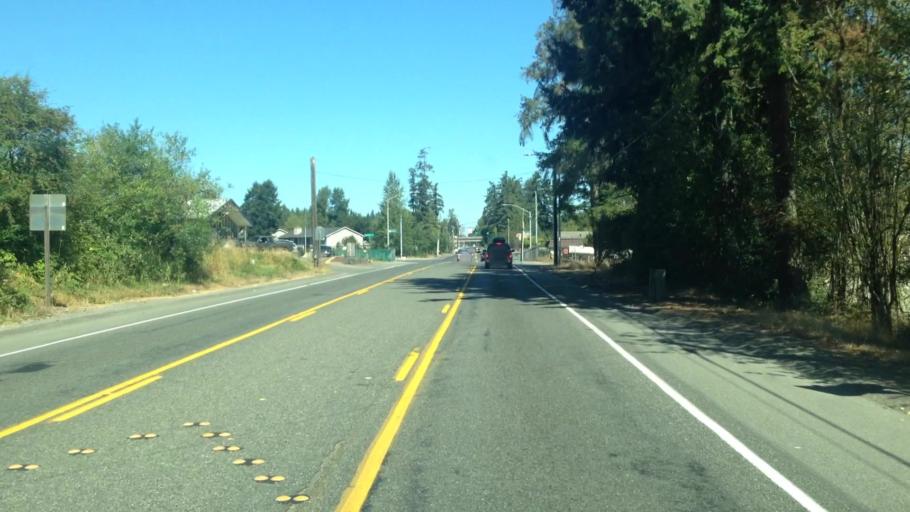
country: US
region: Washington
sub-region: Pierce County
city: Midland
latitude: 47.1535
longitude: -122.4155
